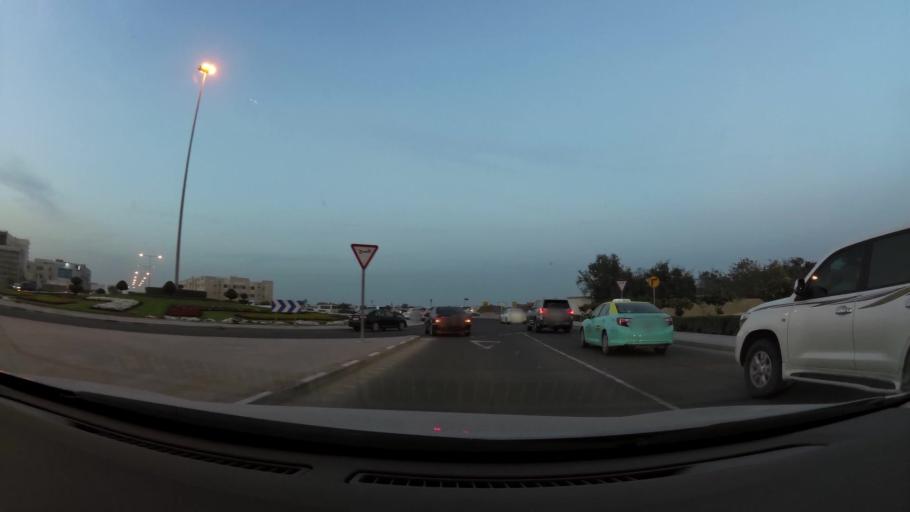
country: QA
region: Al Wakrah
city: Al Wakrah
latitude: 25.1612
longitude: 51.6075
